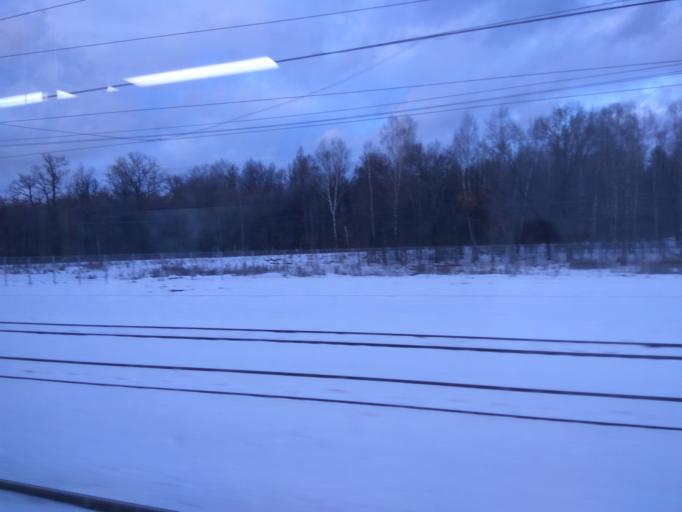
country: RU
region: Moskovskaya
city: Bogorodskoye
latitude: 55.8278
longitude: 37.7063
